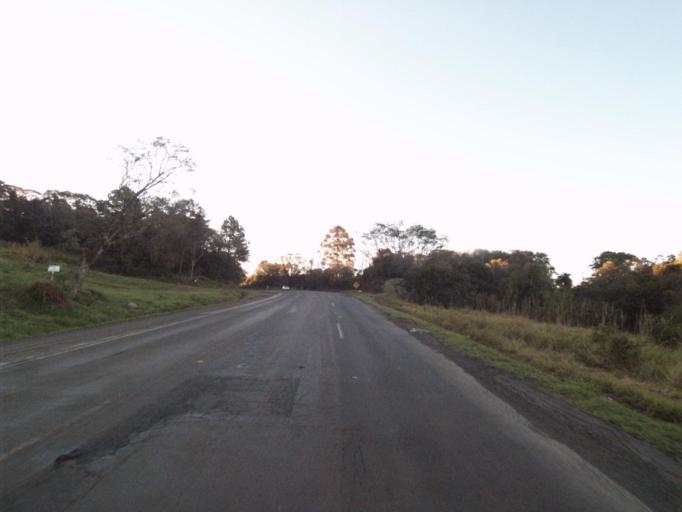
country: BR
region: Santa Catarina
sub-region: Sao Lourenco Do Oeste
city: Sao Lourenco dOeste
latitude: -26.8109
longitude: -53.1678
